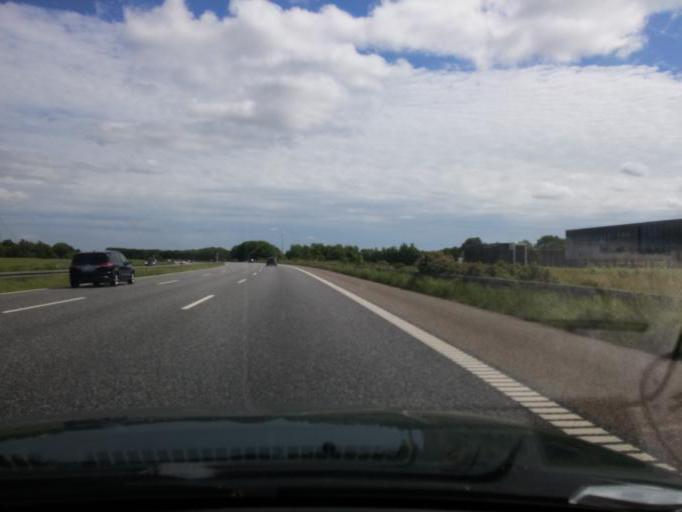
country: DK
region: South Denmark
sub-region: Fredericia Kommune
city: Snoghoj
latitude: 55.5264
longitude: 9.7262
